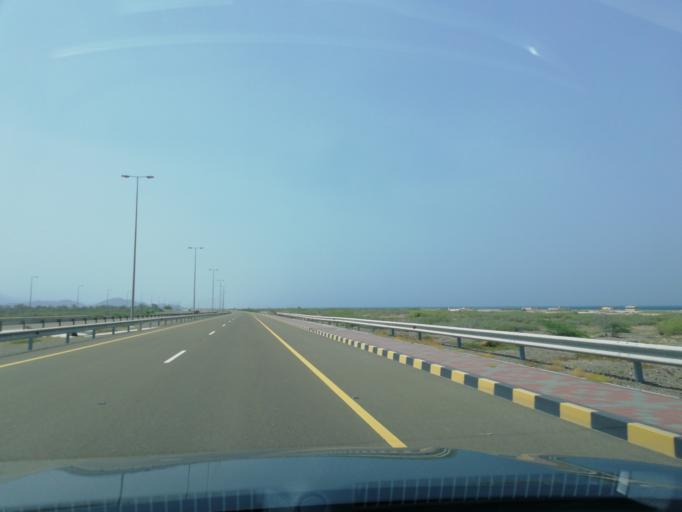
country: OM
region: Al Batinah
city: Shinas
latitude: 24.8864
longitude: 56.4026
